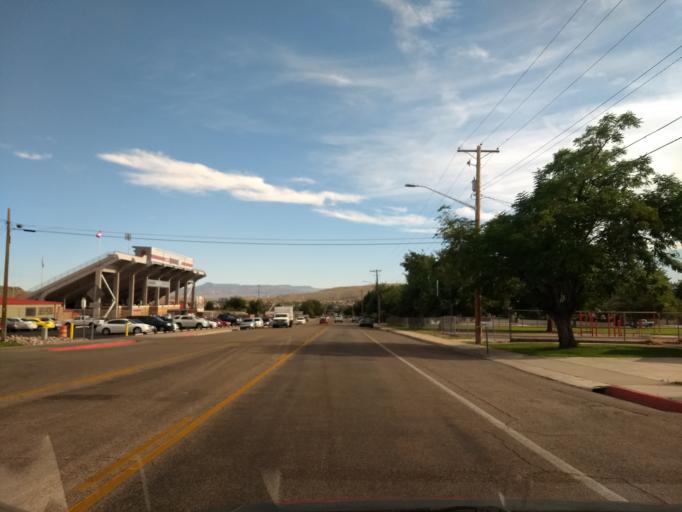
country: US
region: Utah
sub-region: Washington County
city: Saint George
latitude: 37.1008
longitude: -113.5686
